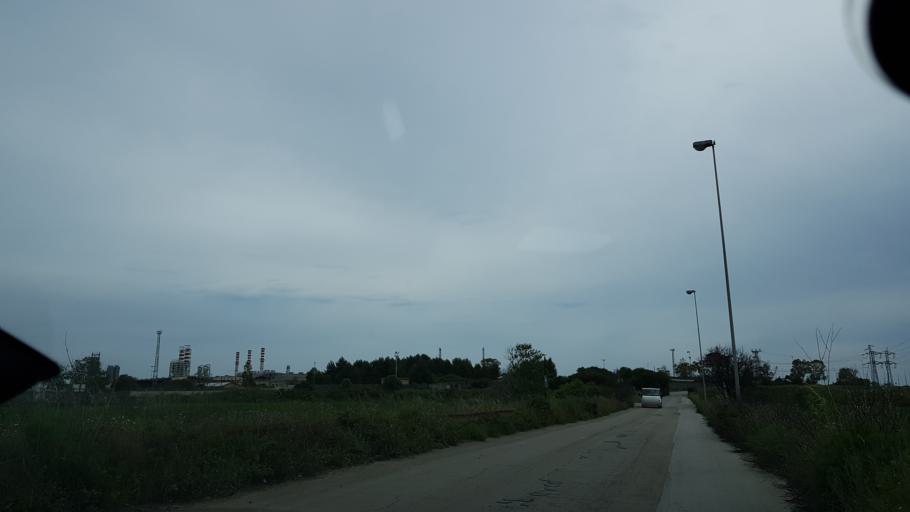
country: IT
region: Apulia
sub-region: Provincia di Brindisi
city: La Rosa
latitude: 40.6261
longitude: 17.9852
